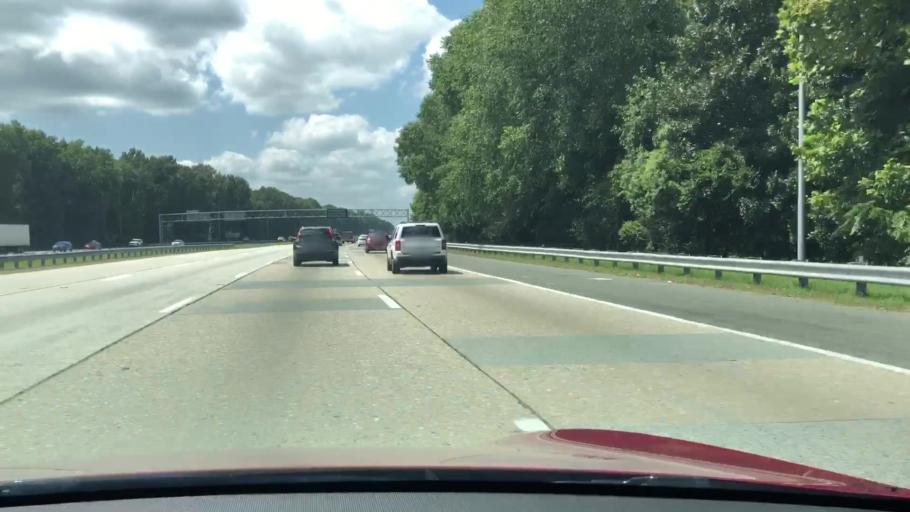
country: US
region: Virginia
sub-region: City of Chesapeake
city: Chesapeake
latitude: 36.8001
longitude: -76.2022
